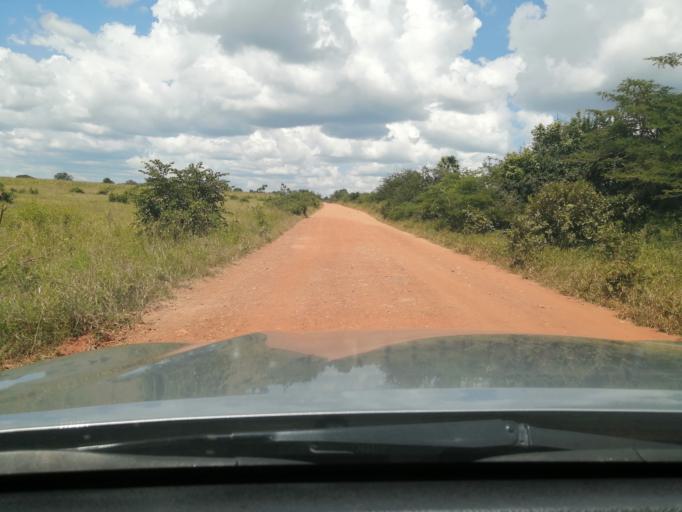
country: ZM
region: Lusaka
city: Lusaka
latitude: -15.1930
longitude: 27.9763
